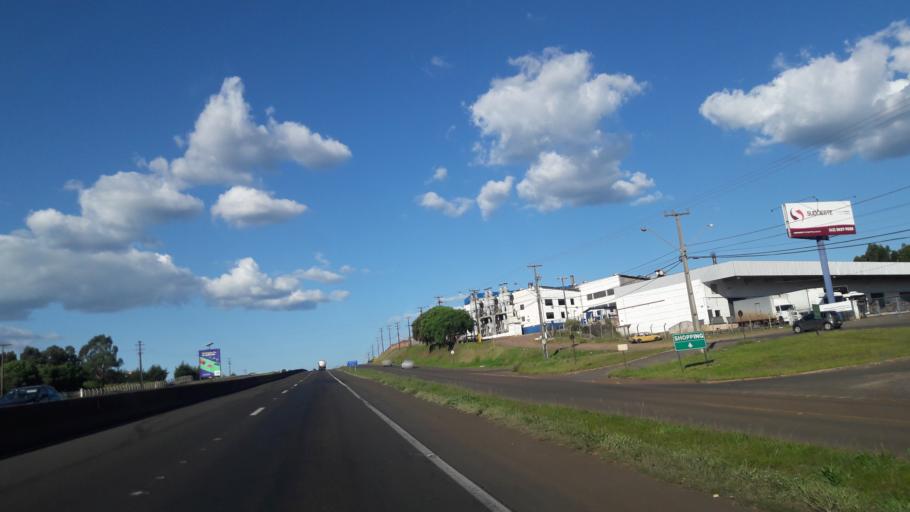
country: BR
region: Parana
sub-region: Guarapuava
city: Guarapuava
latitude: -25.3562
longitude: -51.4621
